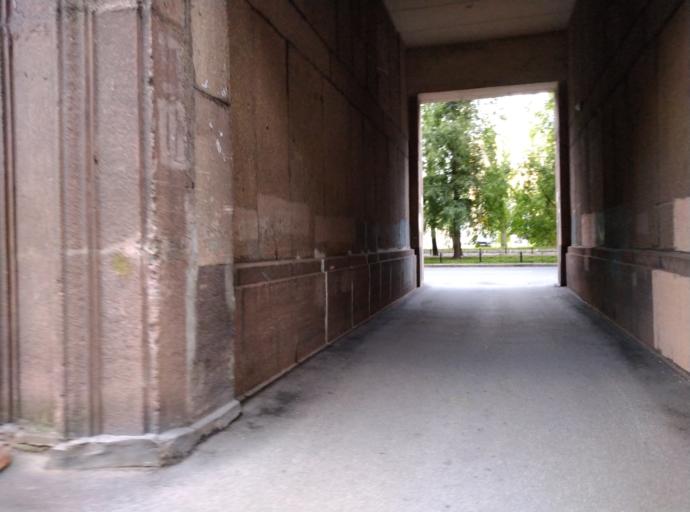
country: RU
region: St.-Petersburg
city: Kupchino
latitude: 59.8588
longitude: 30.3344
